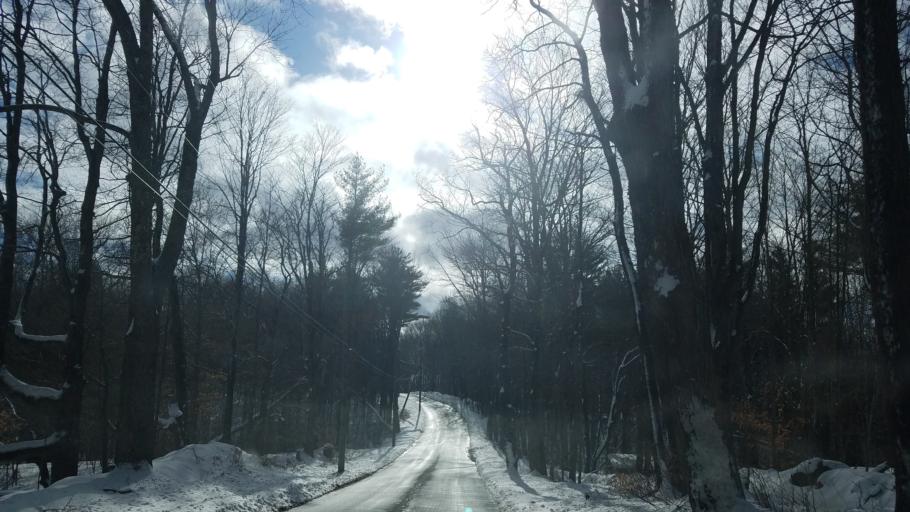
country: US
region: Connecticut
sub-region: Litchfield County
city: Winchester Center
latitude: 41.9788
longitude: -73.1207
